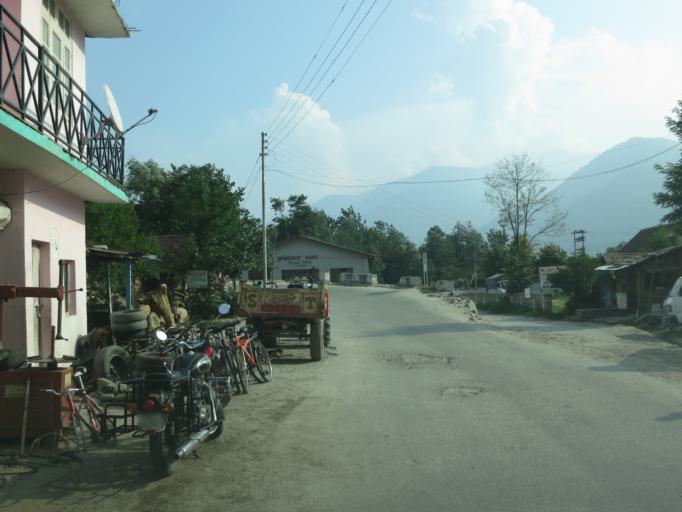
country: IN
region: Himachal Pradesh
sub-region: Kulu
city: Nagar
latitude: 32.1091
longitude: 77.1493
